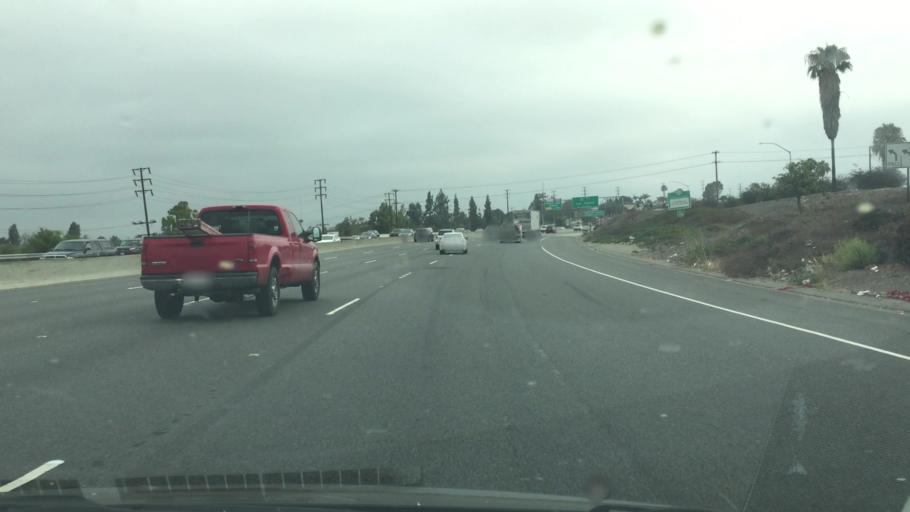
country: US
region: California
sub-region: Orange County
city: Villa Park
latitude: 33.8337
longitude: -117.8354
